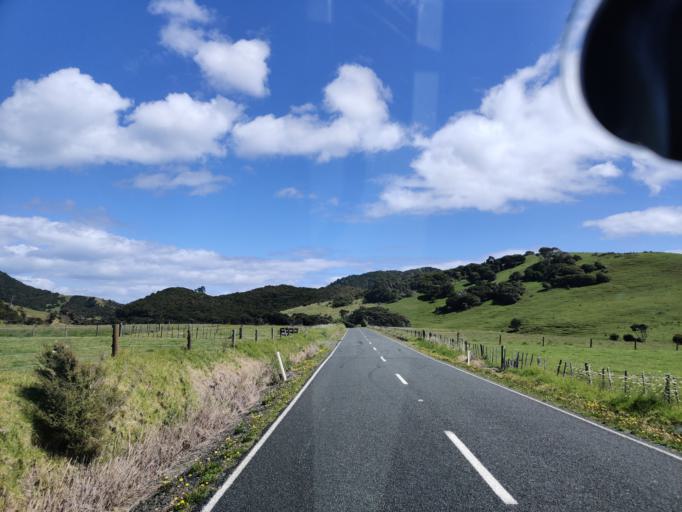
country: NZ
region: Northland
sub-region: Far North District
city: Paihia
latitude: -35.2715
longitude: 174.2791
